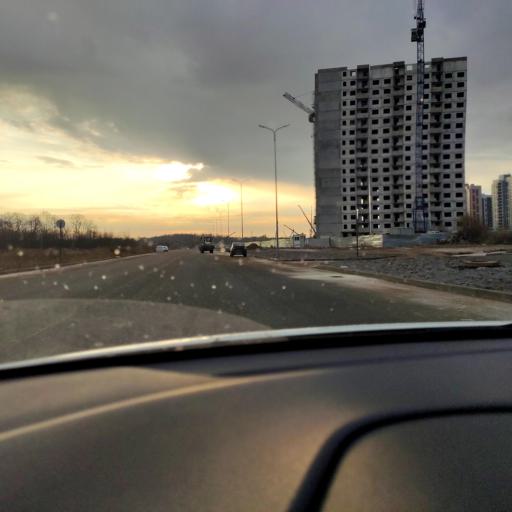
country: RU
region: Tatarstan
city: Osinovo
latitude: 55.8617
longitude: 48.9030
